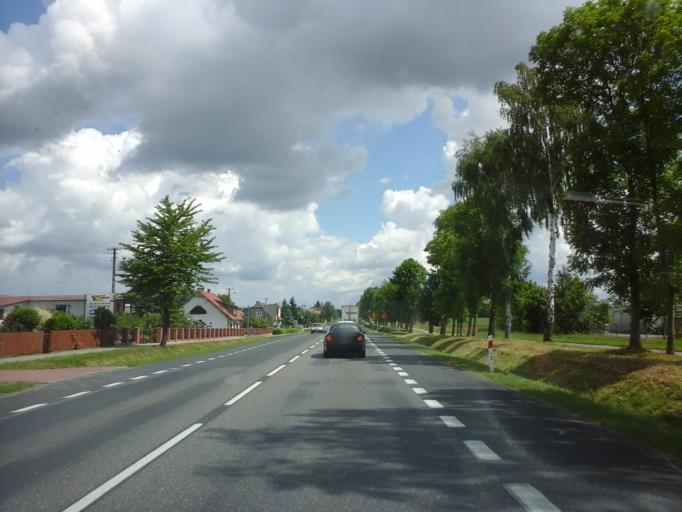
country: PL
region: West Pomeranian Voivodeship
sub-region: Powiat koszalinski
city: Mielno
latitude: 54.1352
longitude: 16.0440
